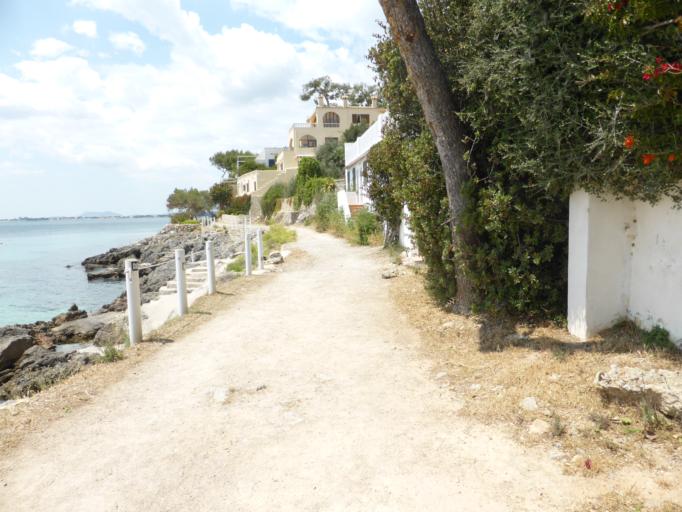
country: ES
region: Balearic Islands
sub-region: Illes Balears
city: Port d'Alcudia
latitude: 39.8368
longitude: 3.1551
